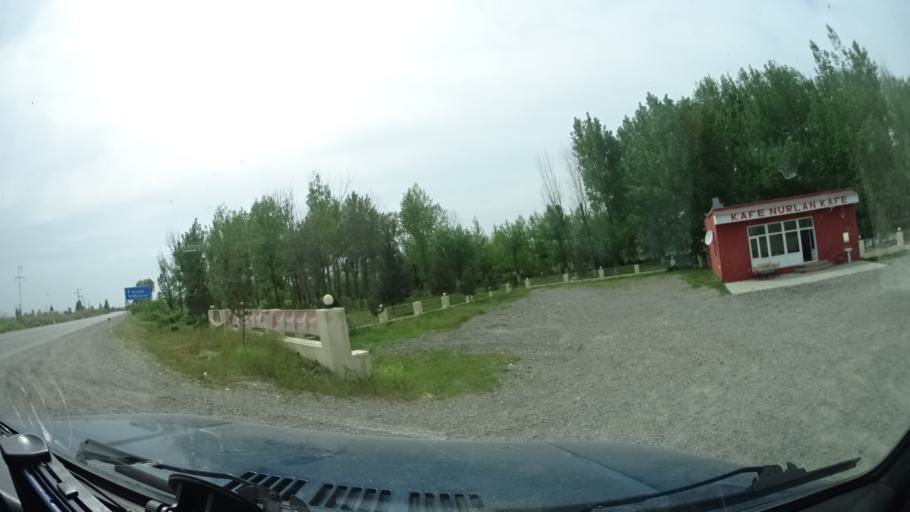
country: AZ
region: Imisli
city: Imishli
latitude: 39.7580
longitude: 47.9995
